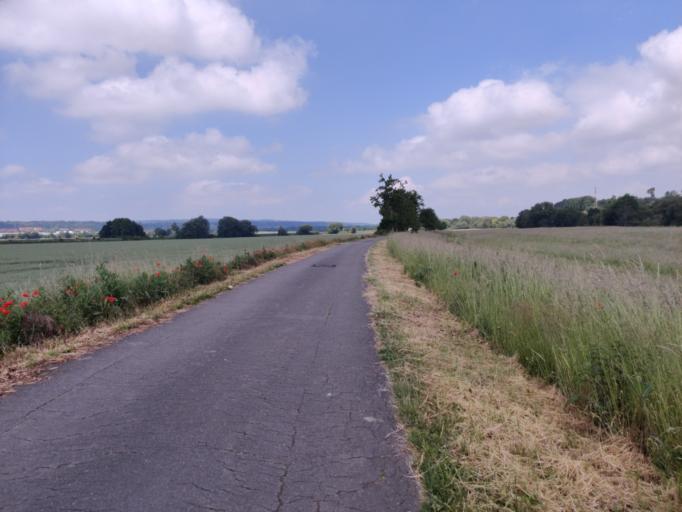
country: DE
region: Lower Saxony
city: Hildesheim
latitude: 52.1200
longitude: 9.9751
